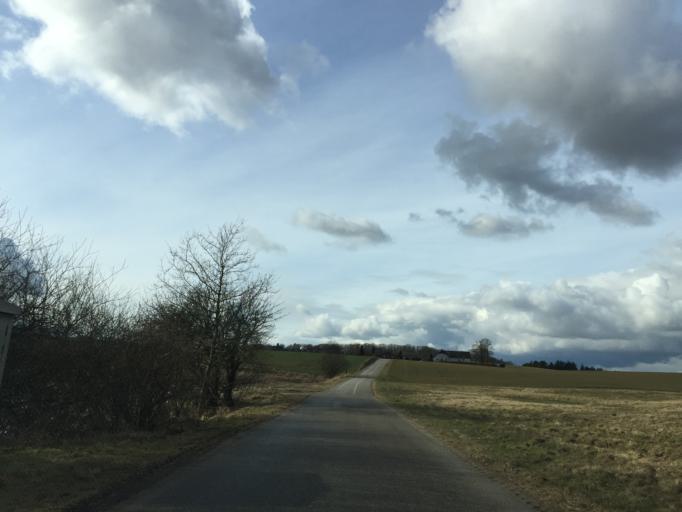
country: DK
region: Central Jutland
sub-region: Favrskov Kommune
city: Hammel
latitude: 56.1984
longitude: 9.7941
